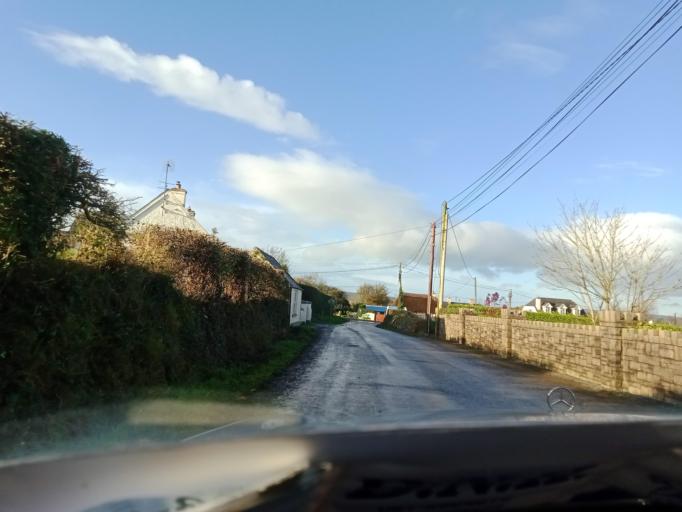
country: IE
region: Leinster
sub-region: Kilkenny
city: Mooncoin
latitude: 52.2735
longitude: -7.2316
